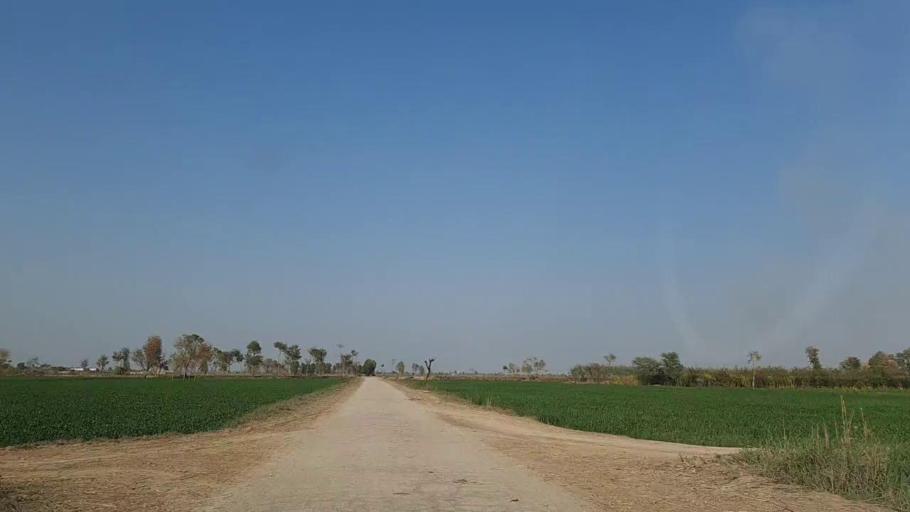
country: PK
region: Sindh
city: Daur
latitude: 26.4664
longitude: 68.3045
